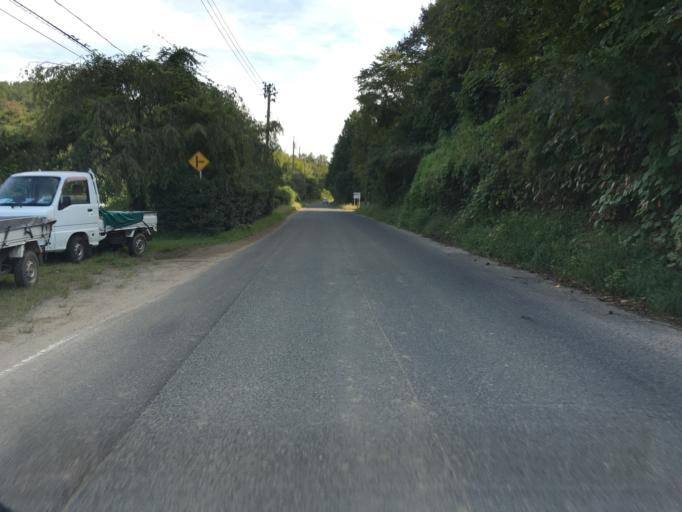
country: JP
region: Fukushima
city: Hobaramachi
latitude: 37.8038
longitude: 140.5900
